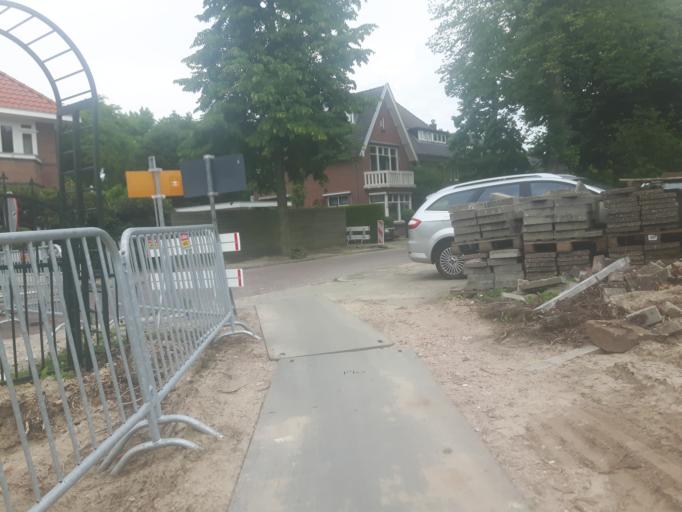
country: NL
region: Overijssel
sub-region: Gemeente Hengelo
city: Hengelo
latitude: 52.2607
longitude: 6.8048
